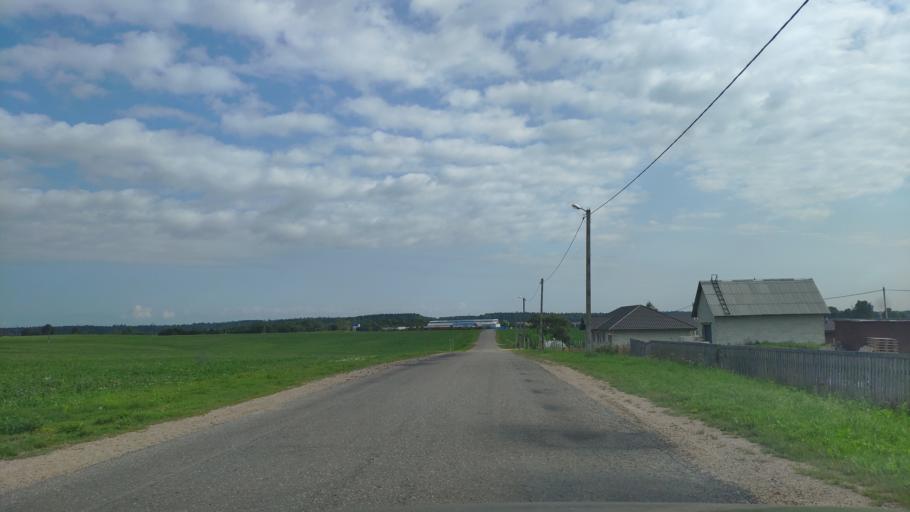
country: BY
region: Minsk
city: Khatsyezhyna
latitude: 53.8568
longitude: 27.3070
